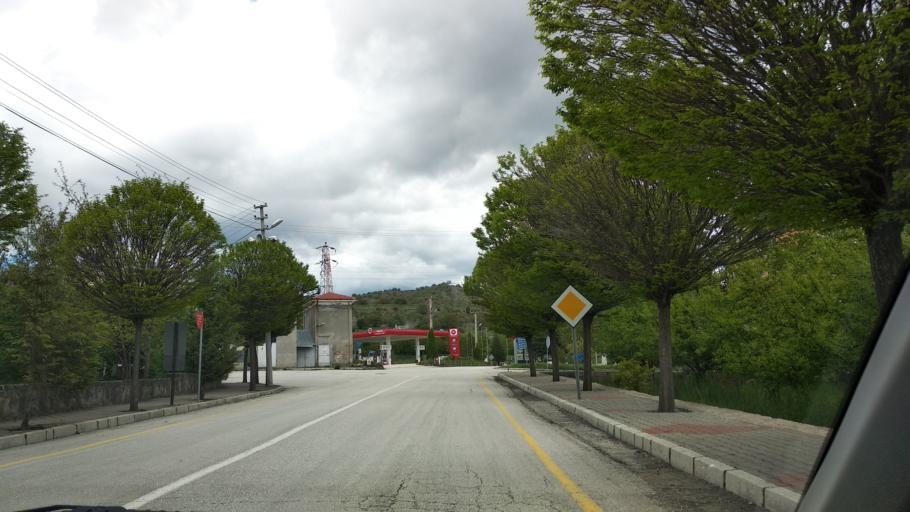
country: TR
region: Bolu
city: Seben
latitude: 40.4153
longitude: 31.5758
